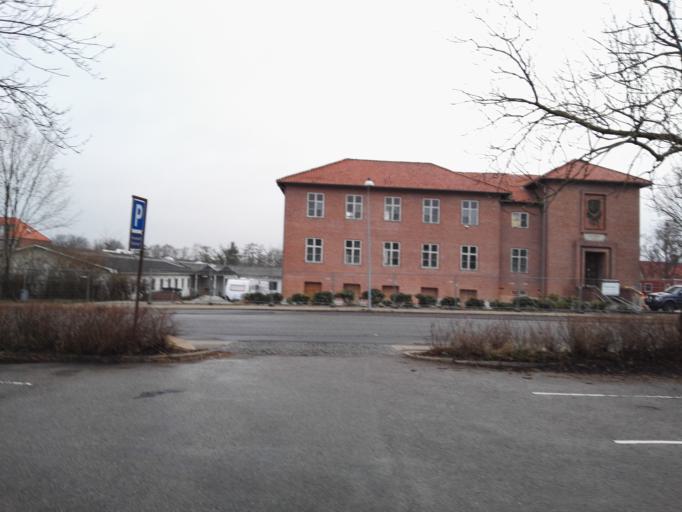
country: DK
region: Capital Region
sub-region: Ballerup Kommune
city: Ballerup
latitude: 55.7311
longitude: 12.3661
